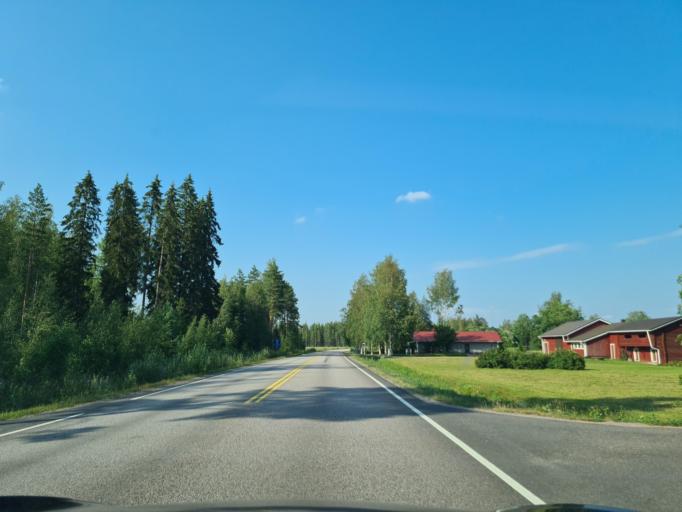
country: FI
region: Satakunta
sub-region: Pohjois-Satakunta
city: Karvia
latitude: 62.1853
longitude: 22.5945
